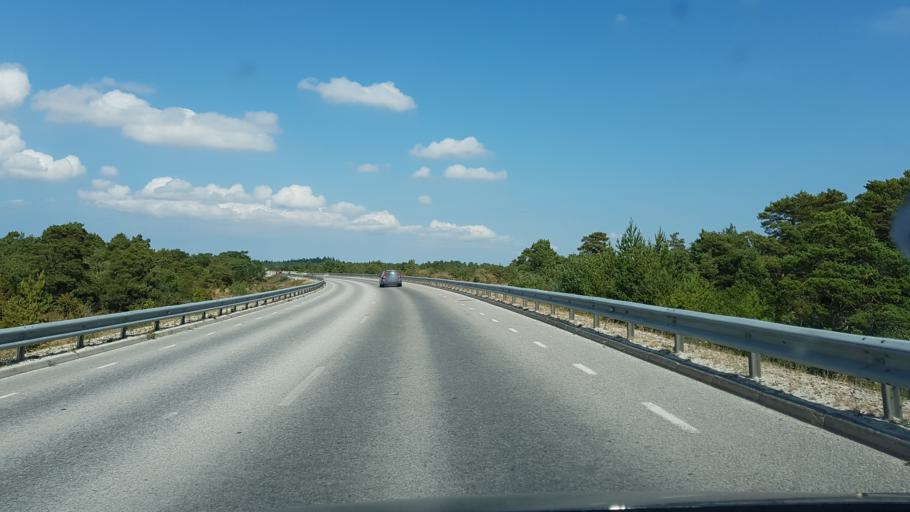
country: SE
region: Gotland
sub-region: Gotland
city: Visby
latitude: 57.6322
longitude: 18.3569
